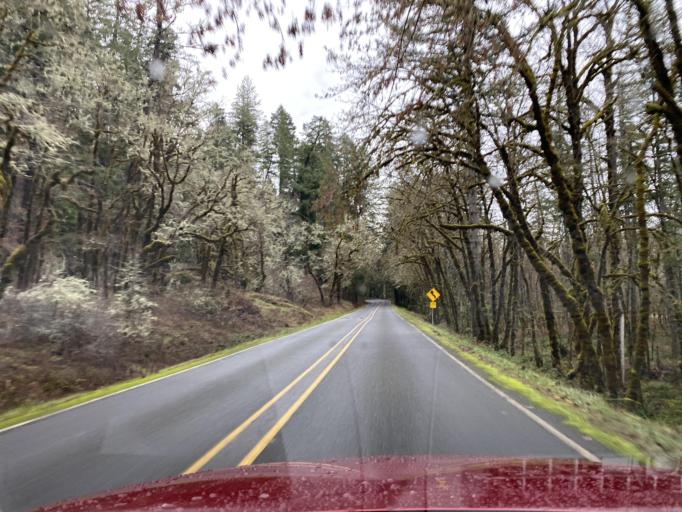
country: US
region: Oregon
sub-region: Lane County
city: Oakridge
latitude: 43.7480
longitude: -122.5181
